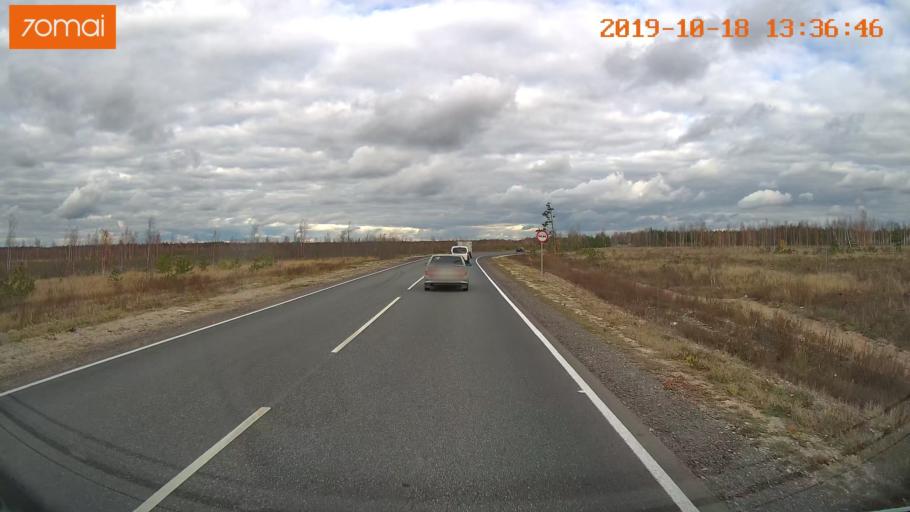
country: RU
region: Rjazan
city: Solotcha
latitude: 54.8739
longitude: 39.9872
